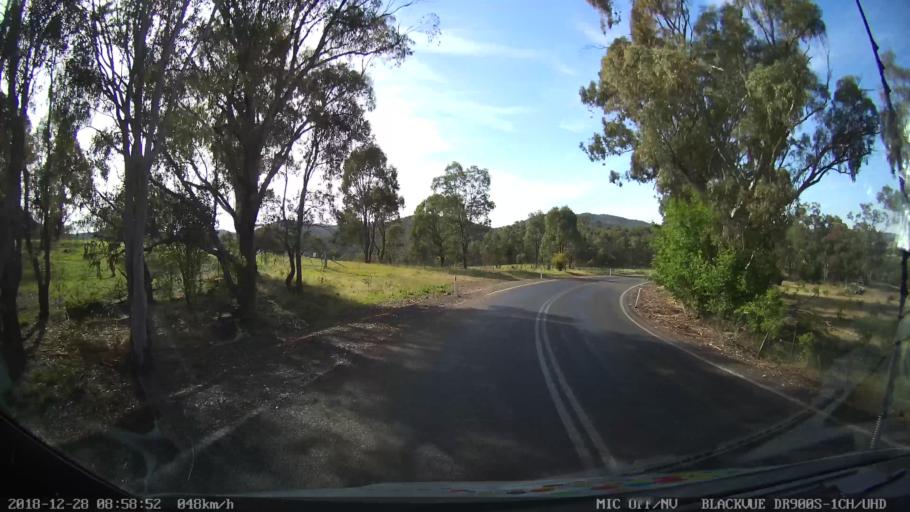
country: AU
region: New South Wales
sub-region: Upper Lachlan Shire
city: Crookwell
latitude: -34.1301
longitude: 149.3328
